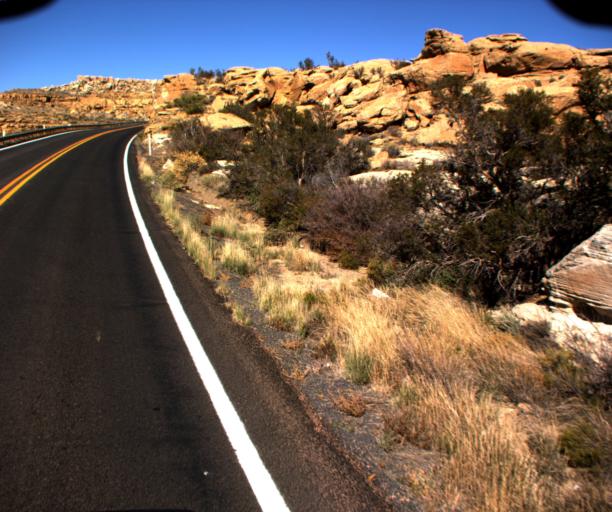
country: US
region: Arizona
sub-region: Navajo County
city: First Mesa
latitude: 35.8831
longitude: -110.6281
